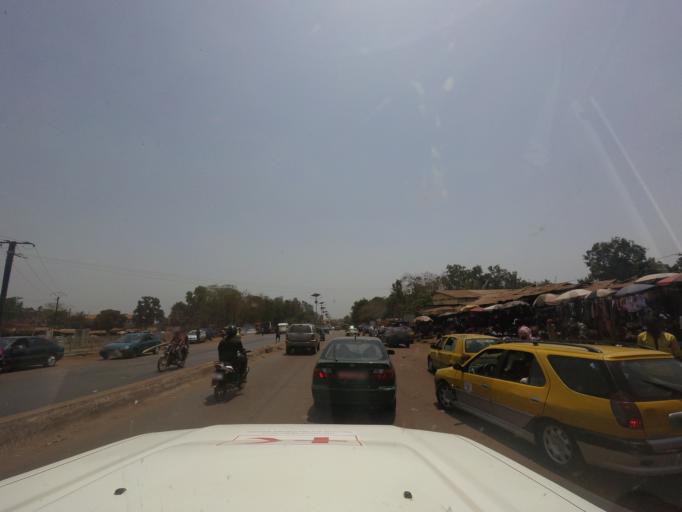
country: GN
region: Conakry
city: Conakry
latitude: 9.6415
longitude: -13.5639
